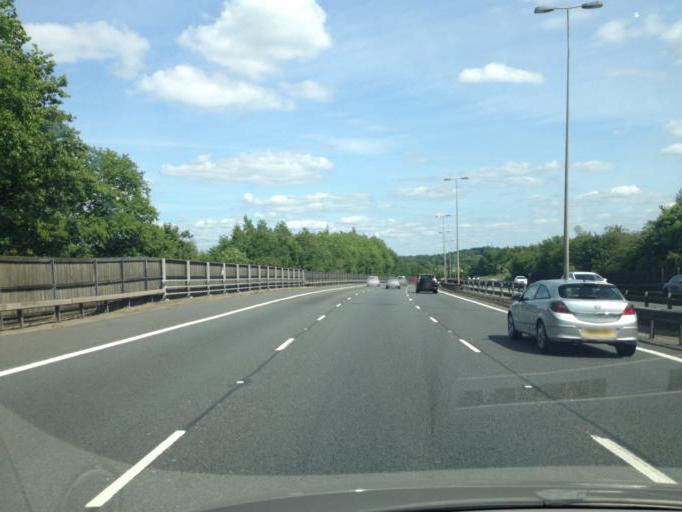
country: GB
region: England
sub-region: Buckinghamshire
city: Stokenchurch
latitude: 51.6271
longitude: -0.8476
